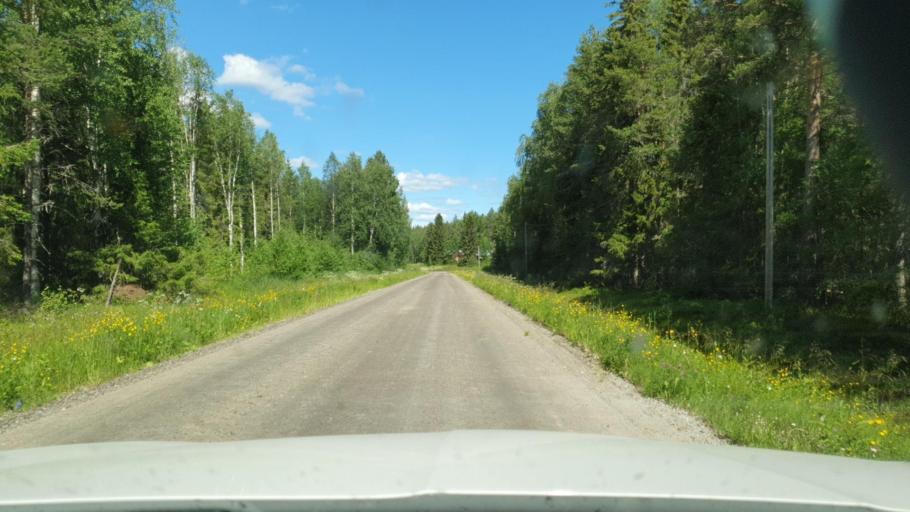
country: SE
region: Vaesterbotten
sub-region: Skelleftea Kommun
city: Backa
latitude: 65.1540
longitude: 21.1605
